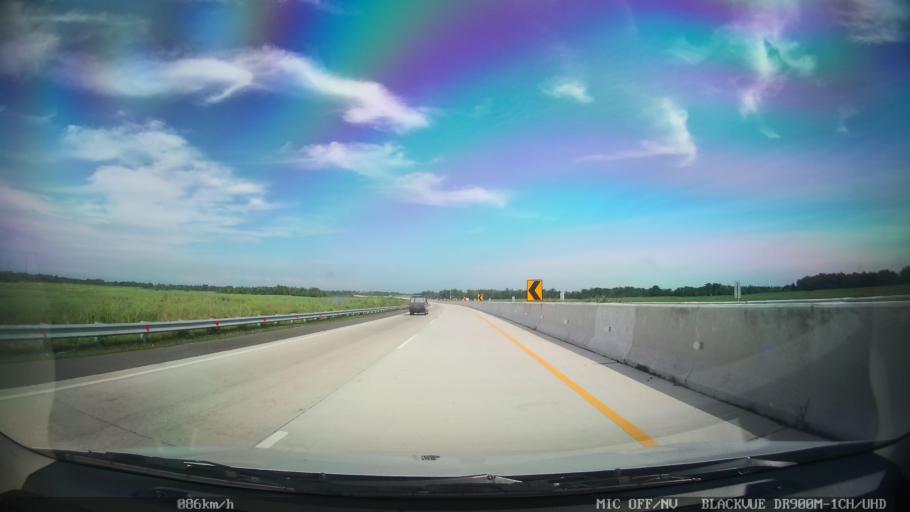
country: ID
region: North Sumatra
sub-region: Kabupaten Langkat
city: Stabat
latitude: 3.7079
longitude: 98.5354
